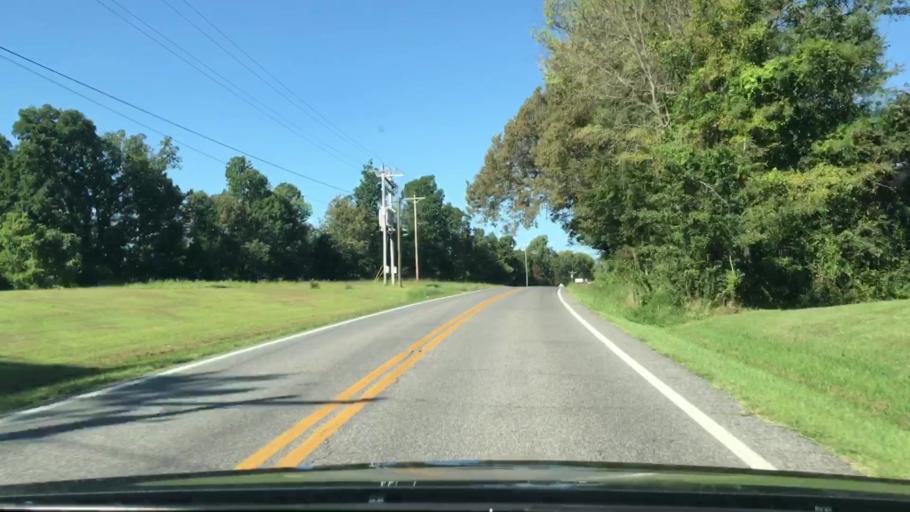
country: US
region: Kentucky
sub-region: Graves County
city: Mayfield
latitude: 36.7664
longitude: -88.5688
